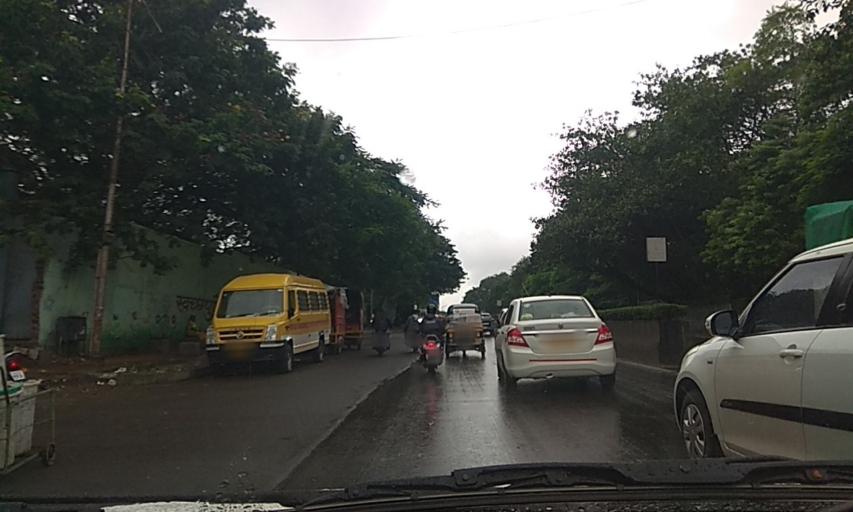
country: IN
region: Maharashtra
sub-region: Pune Division
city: Khadki
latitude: 18.5529
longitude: 73.8867
